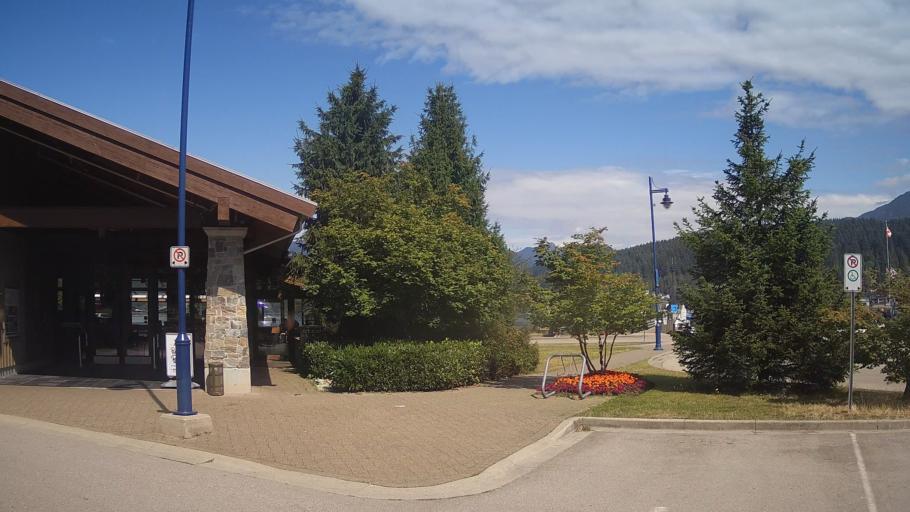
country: CA
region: British Columbia
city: Port Moody
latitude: 49.2808
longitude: -122.8501
